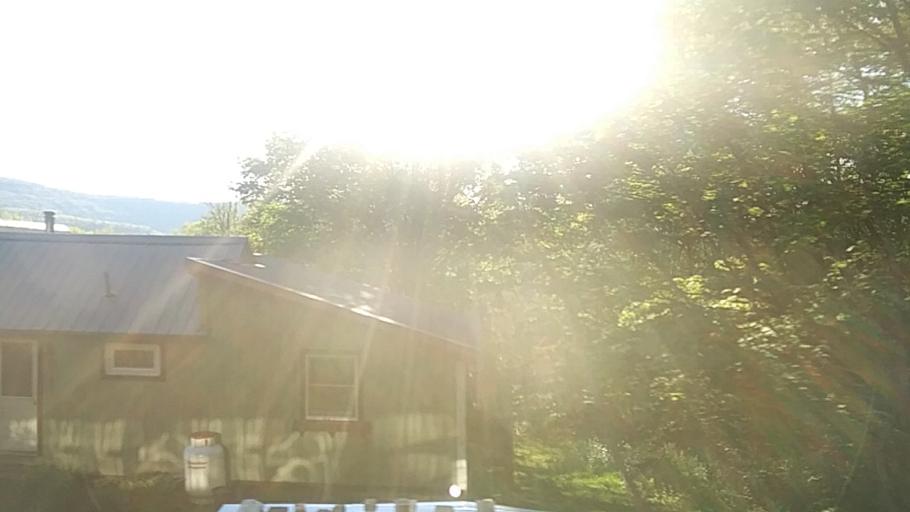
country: US
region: Massachusetts
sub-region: Franklin County
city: Shelburne Falls
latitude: 42.5881
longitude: -72.7447
